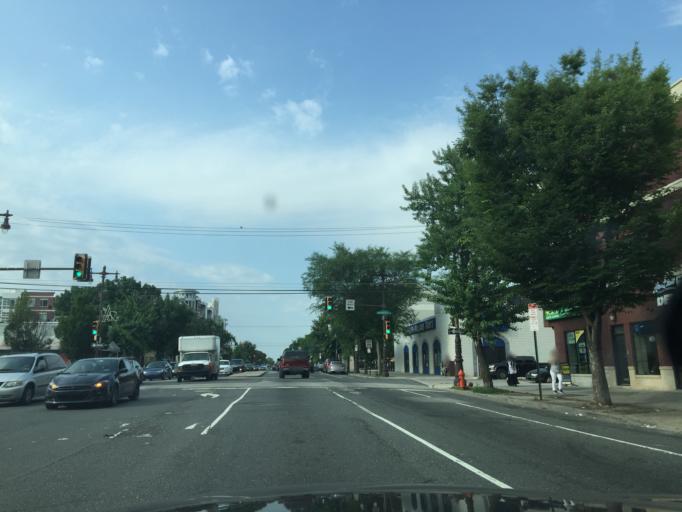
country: US
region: Pennsylvania
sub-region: Philadelphia County
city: Philadelphia
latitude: 39.9432
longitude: -75.1656
